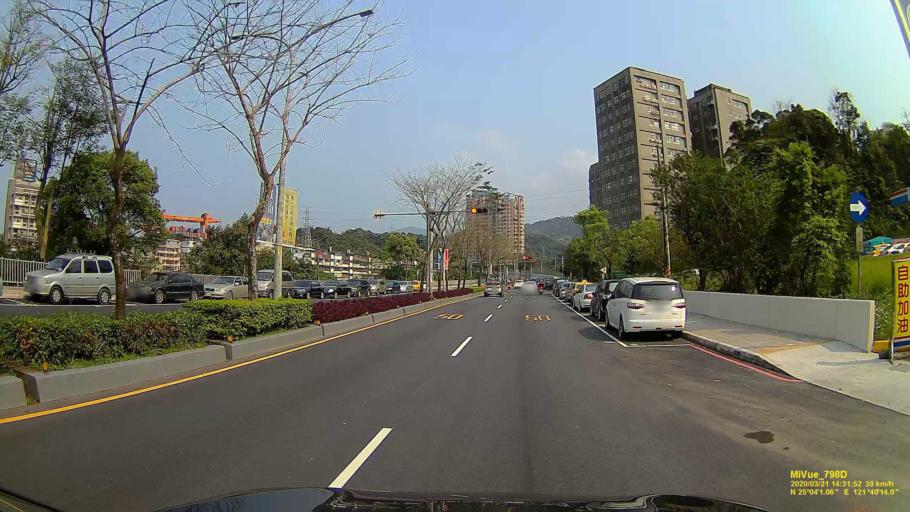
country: TW
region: Taiwan
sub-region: Keelung
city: Keelung
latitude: 25.0669
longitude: 121.6701
